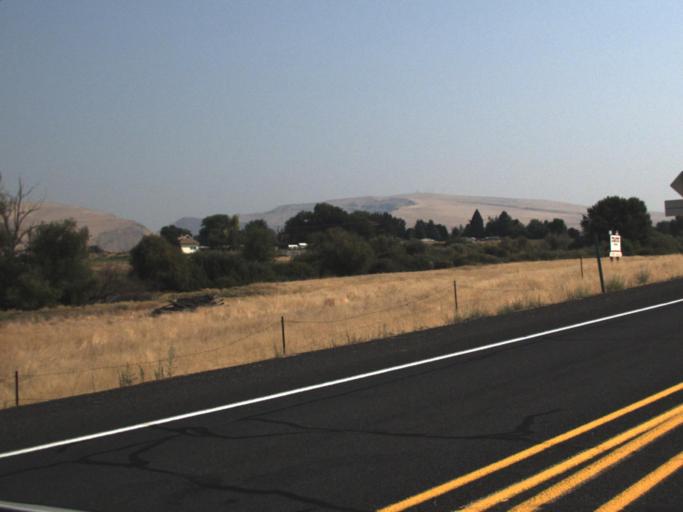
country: US
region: Washington
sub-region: Yakima County
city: Selah
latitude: 46.6806
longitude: -120.4855
